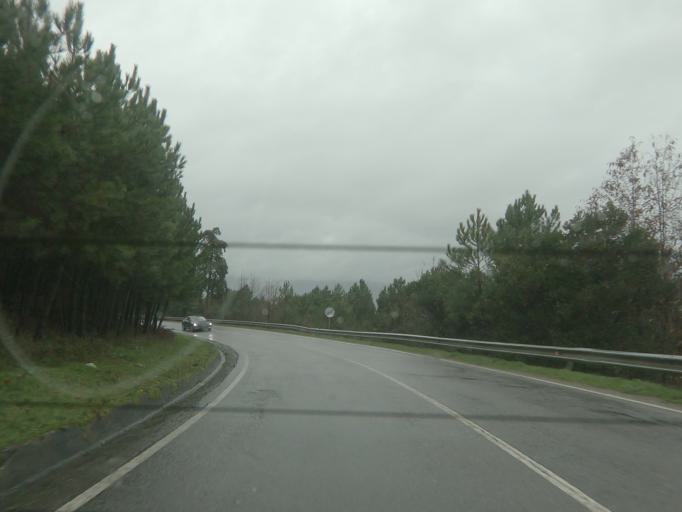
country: PT
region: Vila Real
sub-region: Vila Real
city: Vila Real
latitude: 41.2792
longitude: -7.7174
